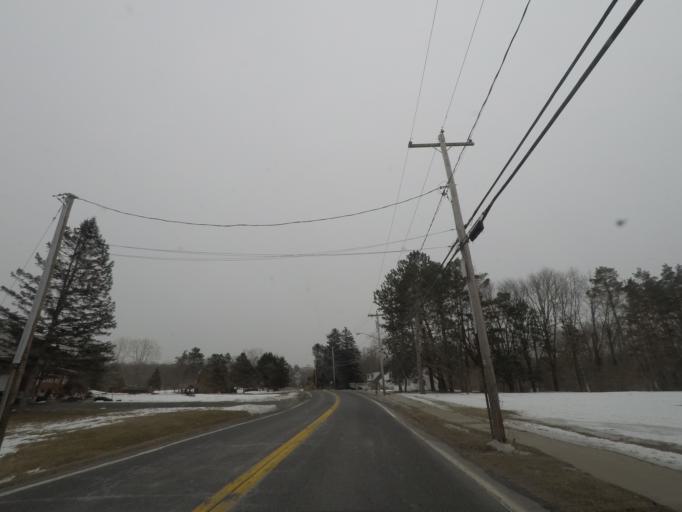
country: US
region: New York
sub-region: Rensselaer County
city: Castleton-on-Hudson
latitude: 42.5473
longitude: -73.8050
